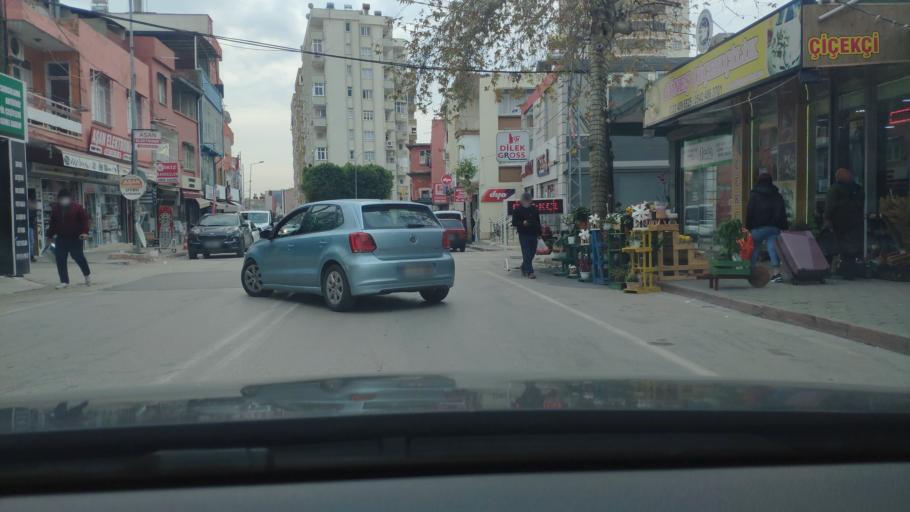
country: TR
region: Adana
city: Adana
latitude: 37.0195
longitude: 35.3140
